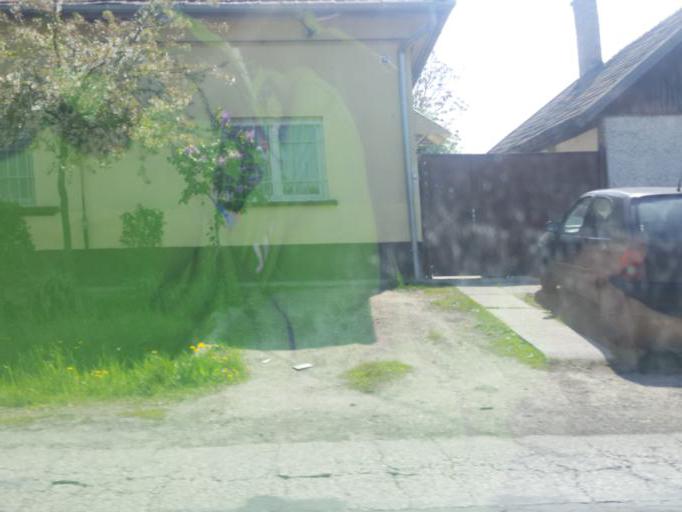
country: HU
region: Pest
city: Monor
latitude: 47.3433
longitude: 19.4447
